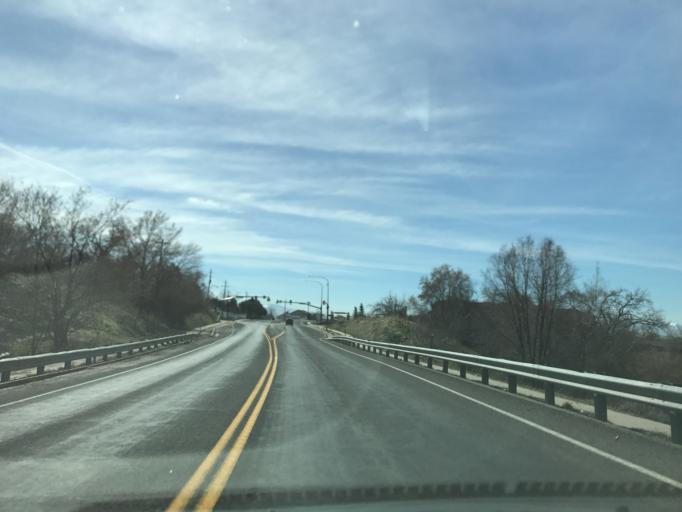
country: US
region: Utah
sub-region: Davis County
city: Layton
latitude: 41.0809
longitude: -111.9509
